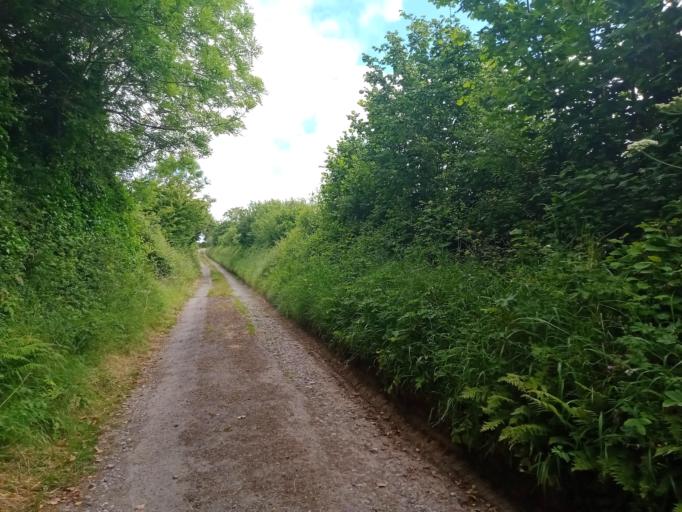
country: IE
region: Leinster
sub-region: Kilkenny
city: Ballyragget
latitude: 52.7796
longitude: -7.4620
